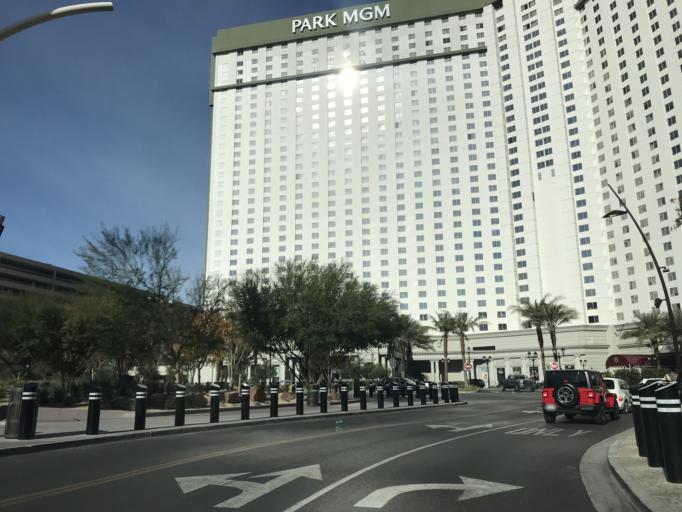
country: US
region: Nevada
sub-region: Clark County
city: Paradise
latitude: 36.1034
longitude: -115.1764
